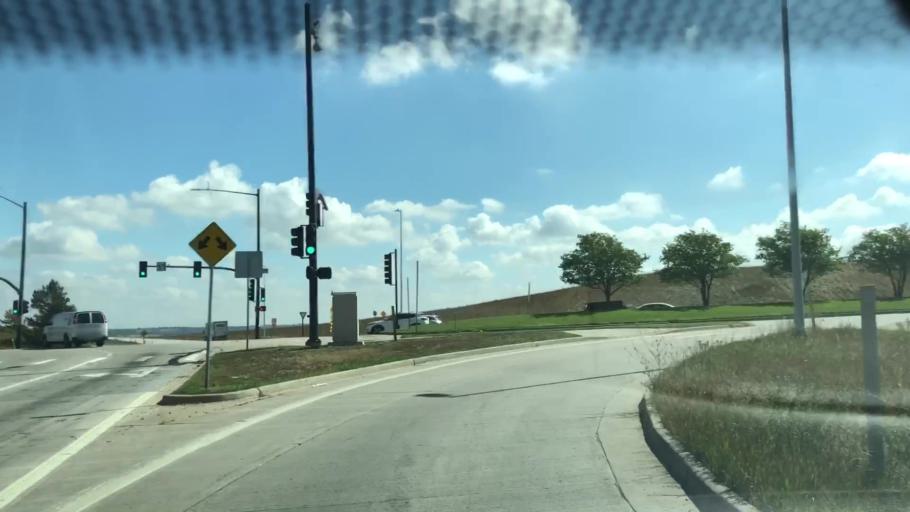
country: US
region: Colorado
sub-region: Douglas County
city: Meridian
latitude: 39.5512
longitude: -104.8400
